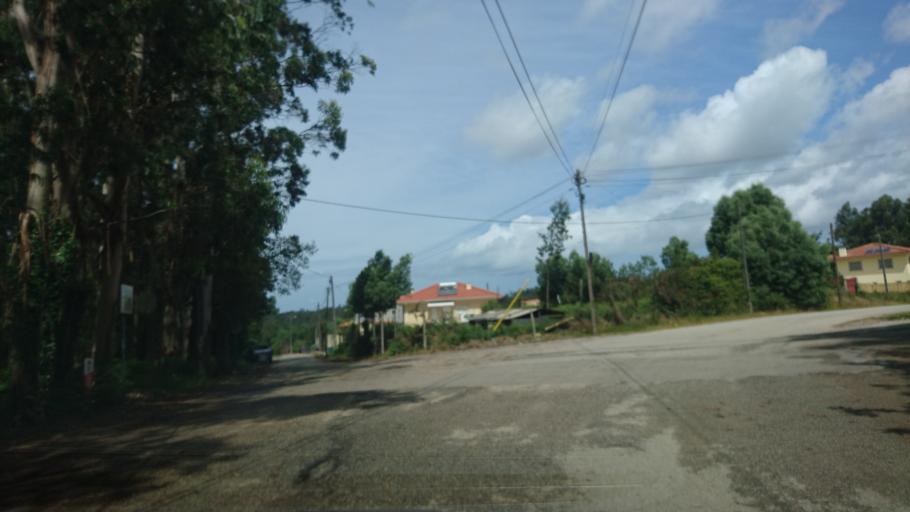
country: PT
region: Aveiro
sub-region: Santa Maria da Feira
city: Rio Meao
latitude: 40.9250
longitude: -8.5859
